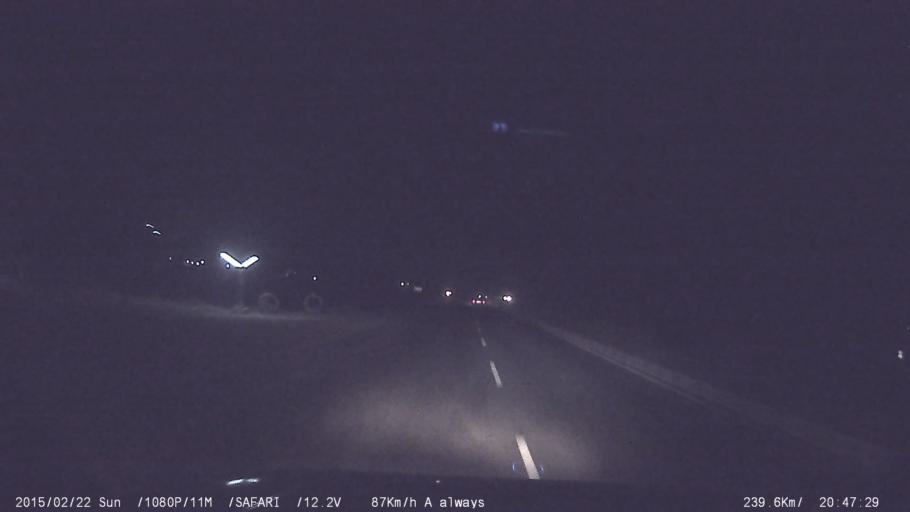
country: IN
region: Tamil Nadu
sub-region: Dindigul
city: Vedasandur
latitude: 10.4954
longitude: 77.9448
